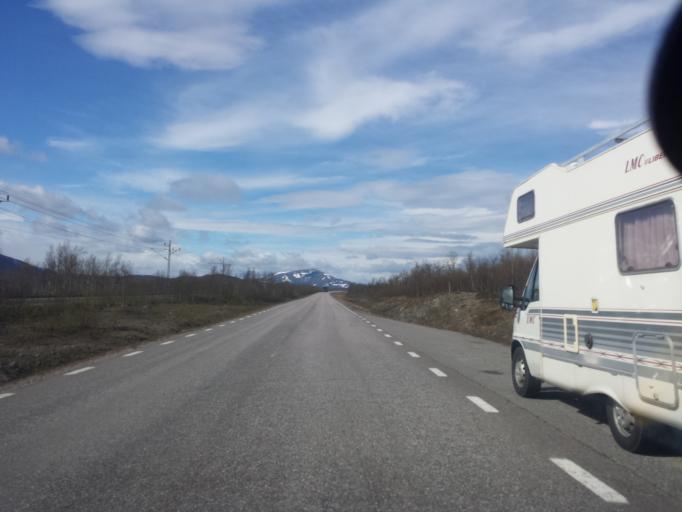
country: SE
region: Norrbotten
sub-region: Kiruna Kommun
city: Kiruna
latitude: 68.0566
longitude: 19.8275
